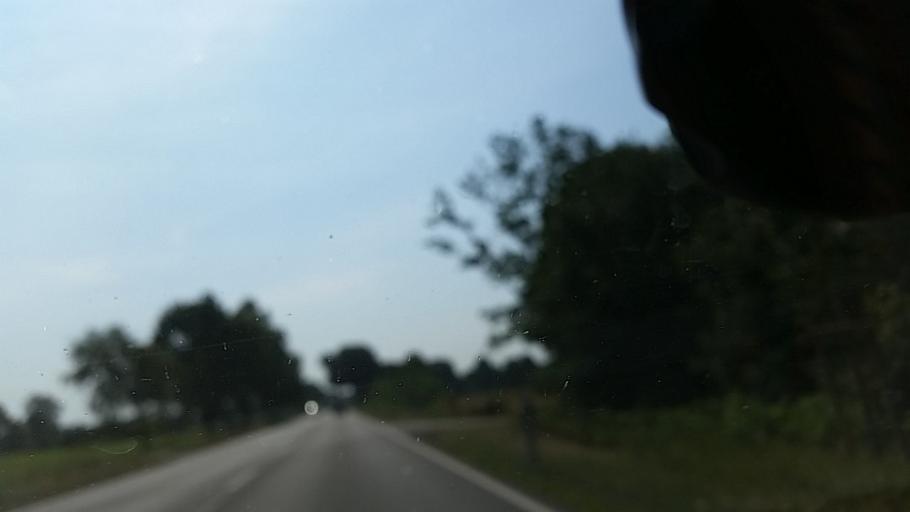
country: DE
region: Lower Saxony
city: Diepholz
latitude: 52.6108
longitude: 8.3240
